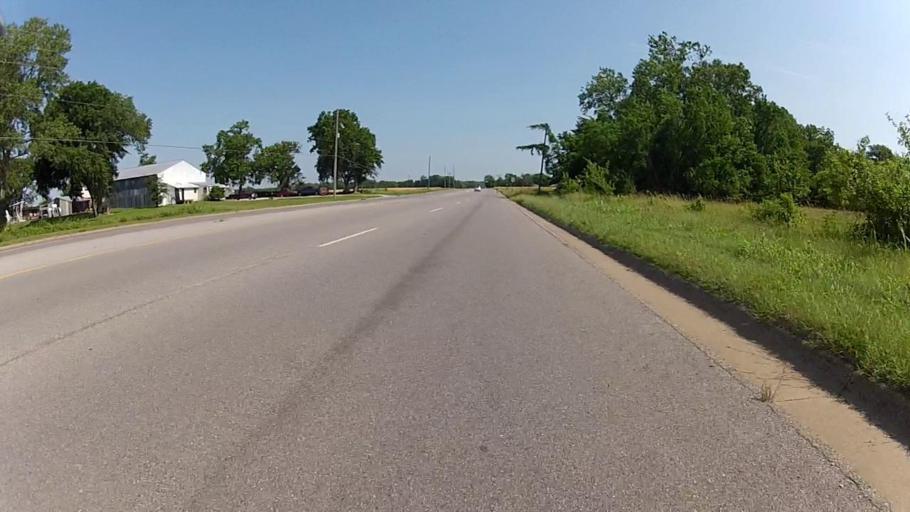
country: US
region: Kansas
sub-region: Montgomery County
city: Independence
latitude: 37.2074
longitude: -95.7106
